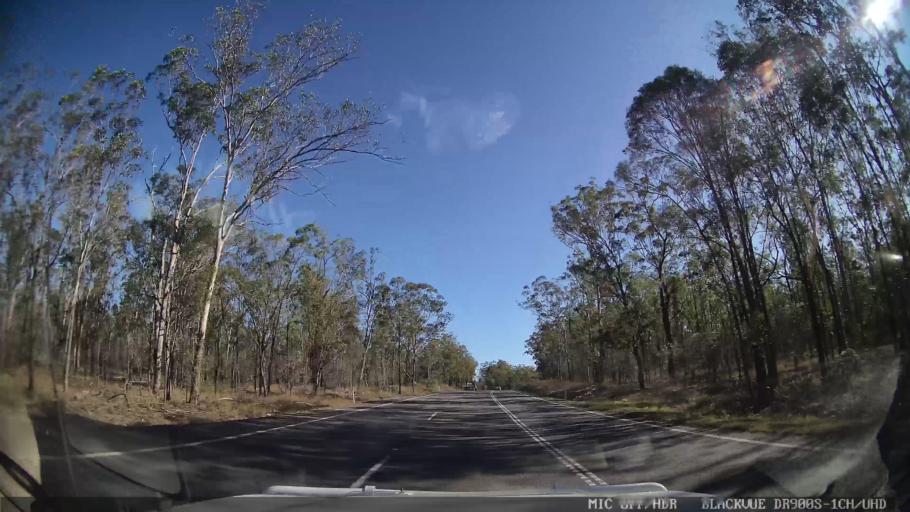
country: AU
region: Queensland
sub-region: Bundaberg
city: Childers
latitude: -25.2146
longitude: 152.0795
